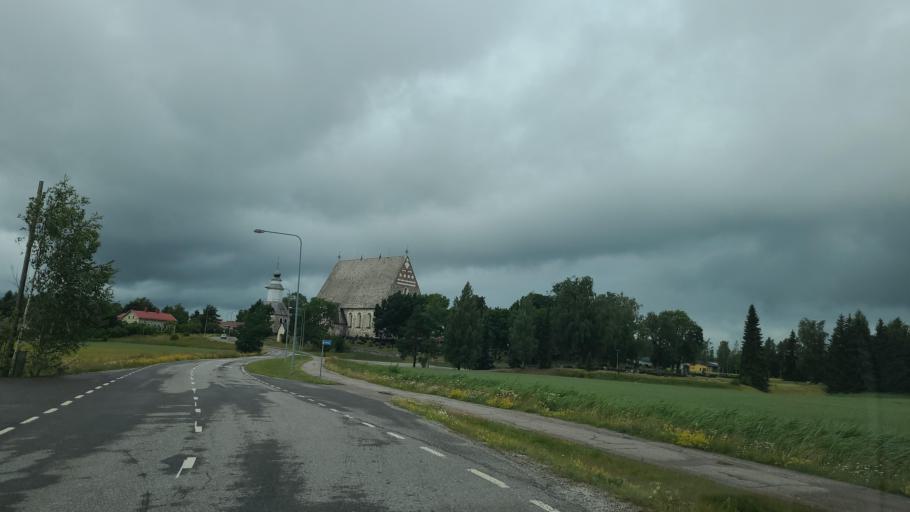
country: FI
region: Varsinais-Suomi
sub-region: Turku
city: Sauvo
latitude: 60.3415
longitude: 22.7029
